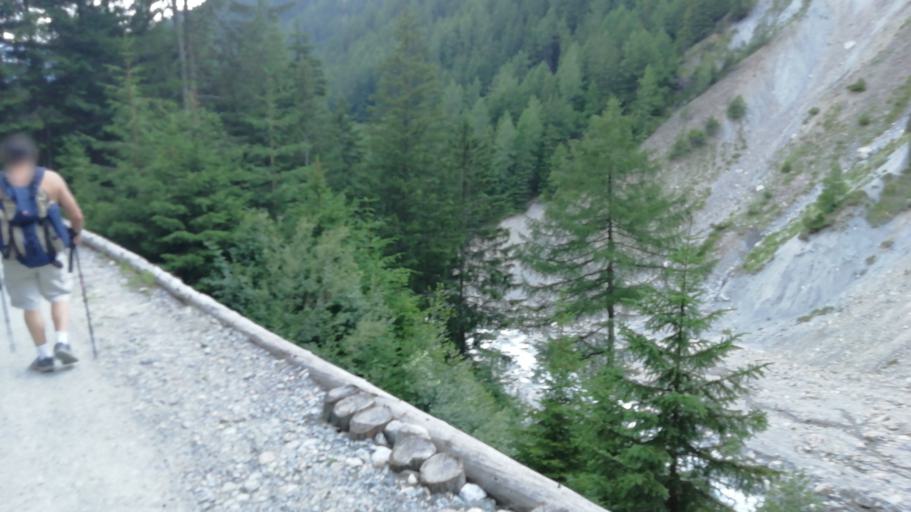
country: IT
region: Lombardy
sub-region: Provincia di Sondrio
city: Sant'Antonio
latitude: 46.4753
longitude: 10.4518
